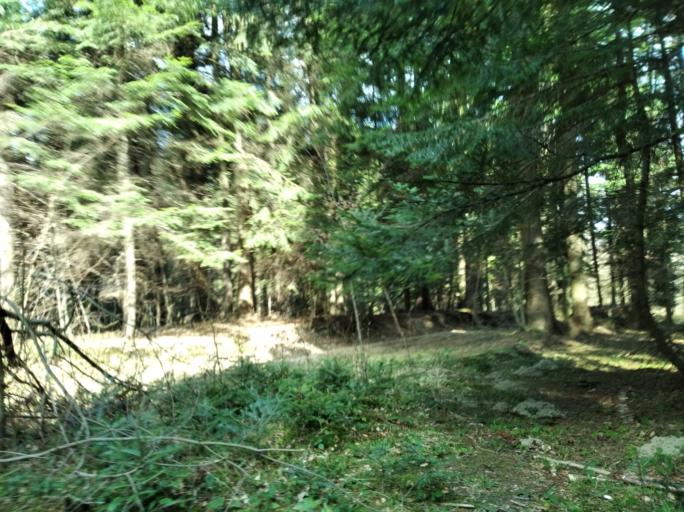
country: PL
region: Subcarpathian Voivodeship
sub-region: Powiat strzyzowski
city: Strzyzow
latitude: 49.8256
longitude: 21.8012
